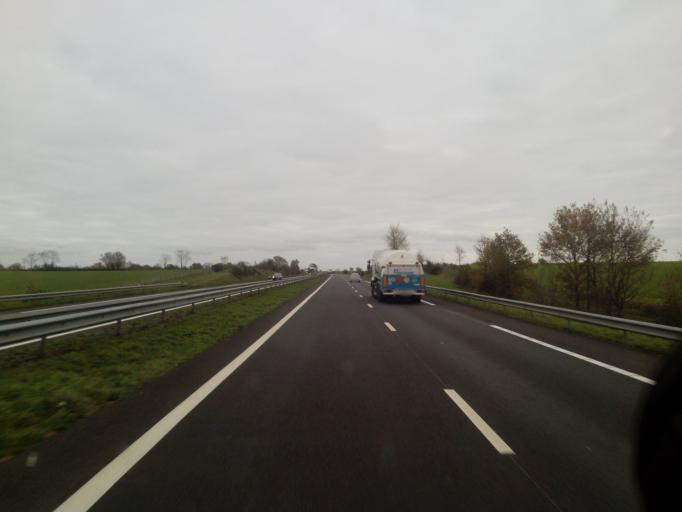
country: FR
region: Pays de la Loire
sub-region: Departement de Maine-et-Loire
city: Saint-Andre-de-la-Marche
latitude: 47.0838
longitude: -0.9736
